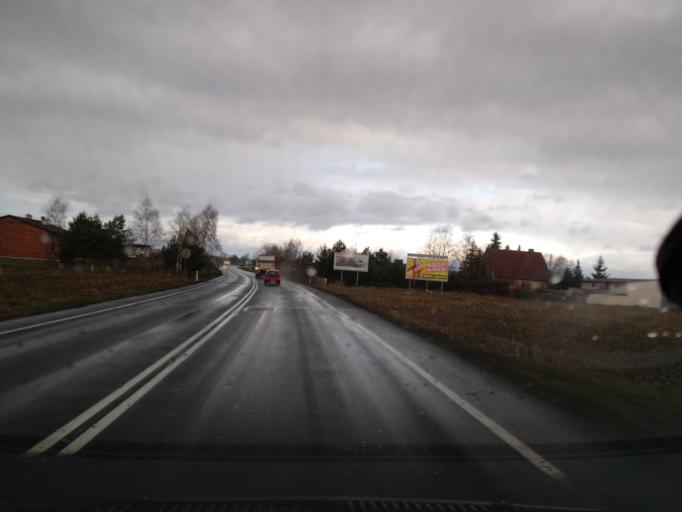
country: PL
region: Greater Poland Voivodeship
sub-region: Powiat koninski
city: Stare Miasto
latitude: 52.1547
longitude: 18.2055
